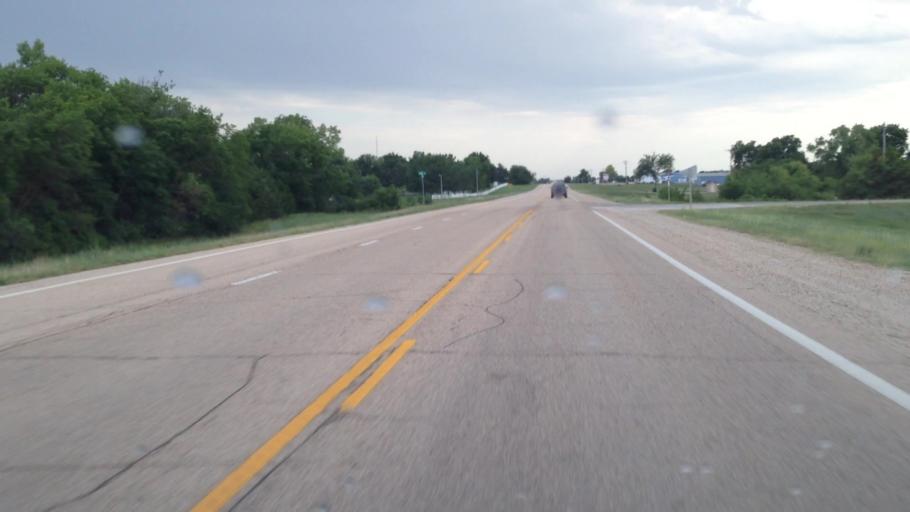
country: US
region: Kansas
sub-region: Coffey County
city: Burlington
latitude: 38.1837
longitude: -95.7388
